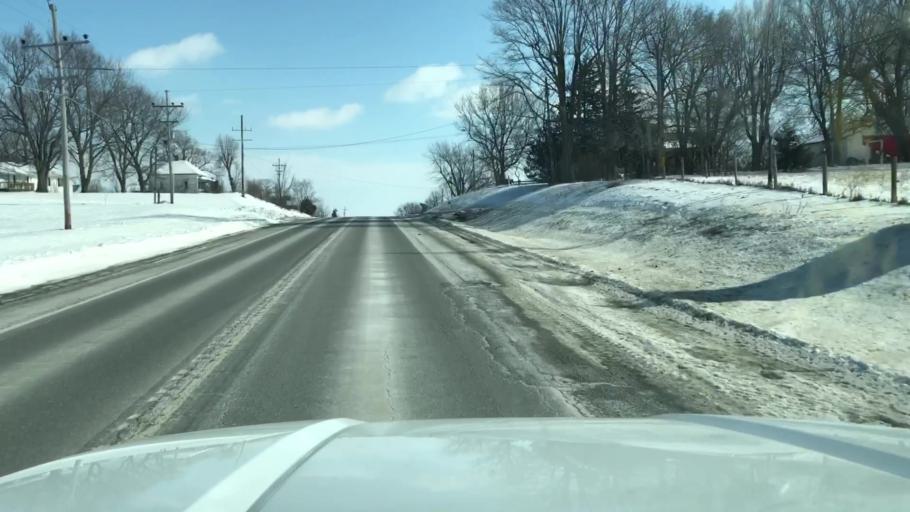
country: US
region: Missouri
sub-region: Nodaway County
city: Maryville
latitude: 40.3446
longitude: -94.7953
